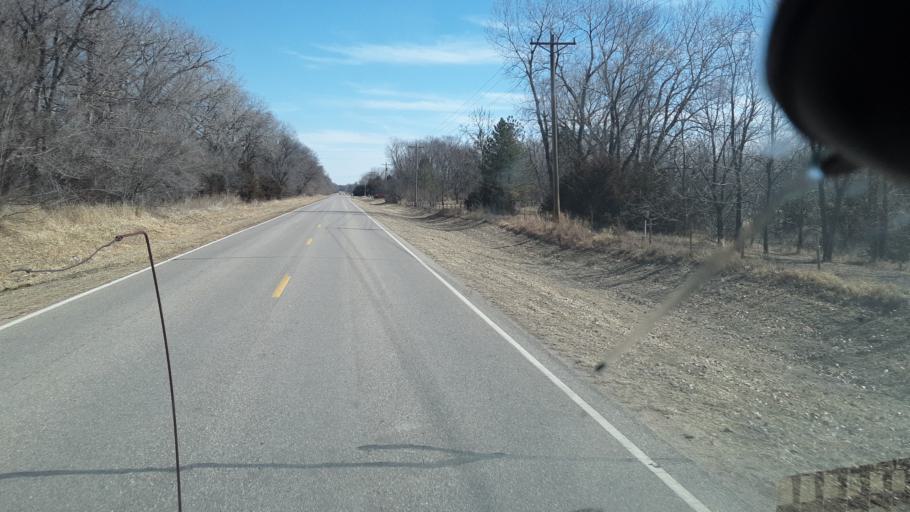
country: US
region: Kansas
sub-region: Reno County
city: Buhler
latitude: 38.1593
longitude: -97.8751
